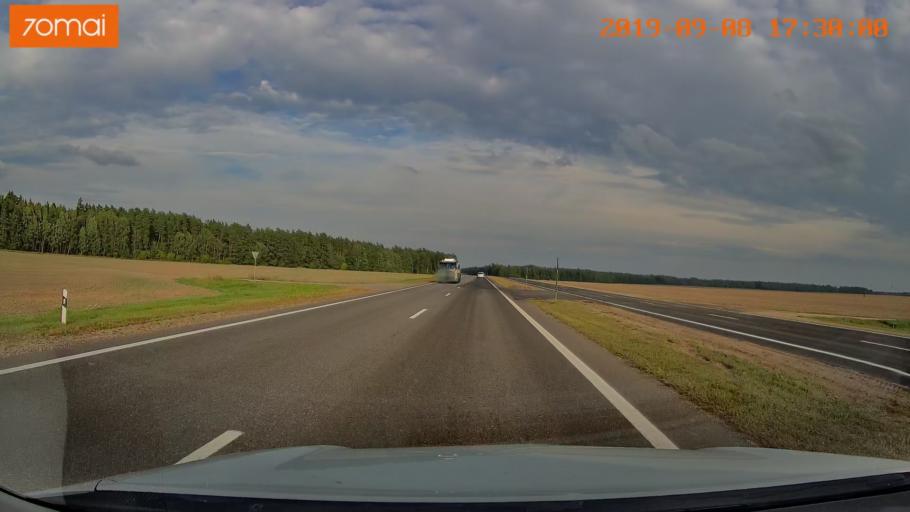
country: BY
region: Grodnenskaya
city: Skidal'
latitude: 53.5844
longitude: 24.4405
